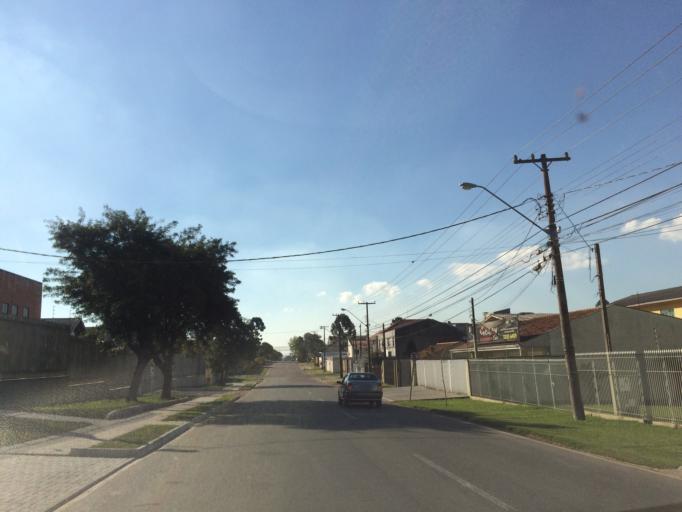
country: BR
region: Parana
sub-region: Sao Jose Dos Pinhais
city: Sao Jose dos Pinhais
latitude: -25.5092
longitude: -49.2324
